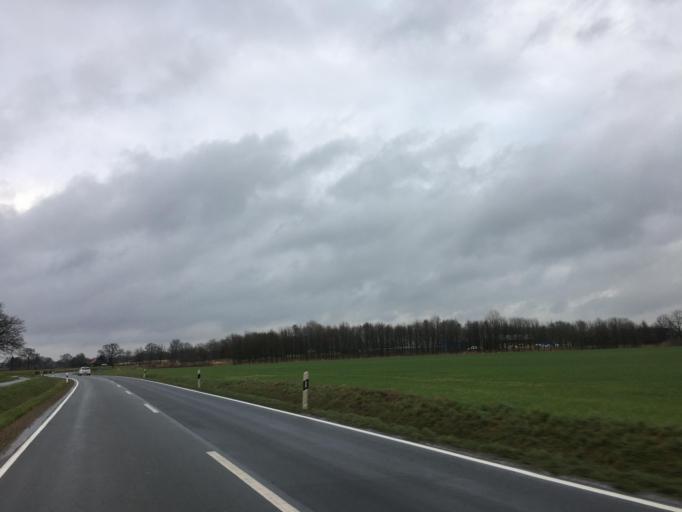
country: DE
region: North Rhine-Westphalia
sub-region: Regierungsbezirk Munster
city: Nordwalde
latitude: 52.1024
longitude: 7.4774
